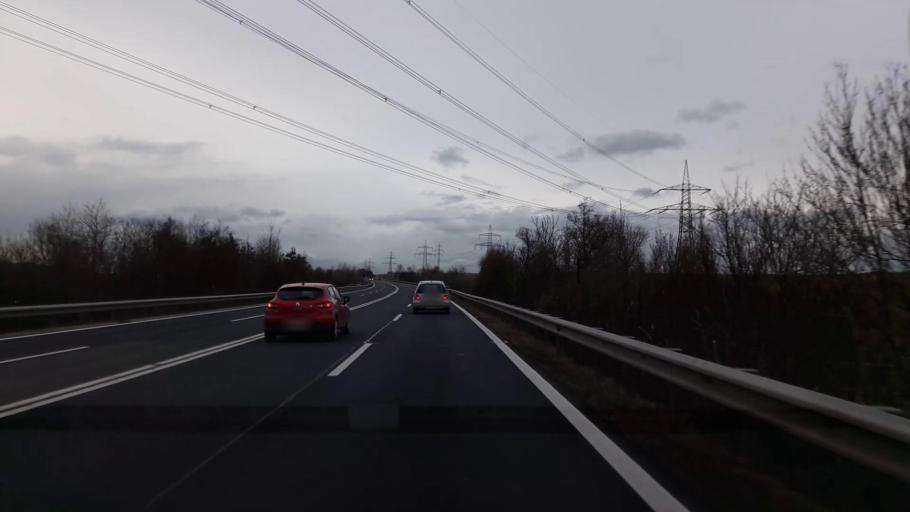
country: AT
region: Burgenland
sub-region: Politischer Bezirk Oberpullendorf
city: Weppersdorf
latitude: 47.5866
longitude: 16.4146
